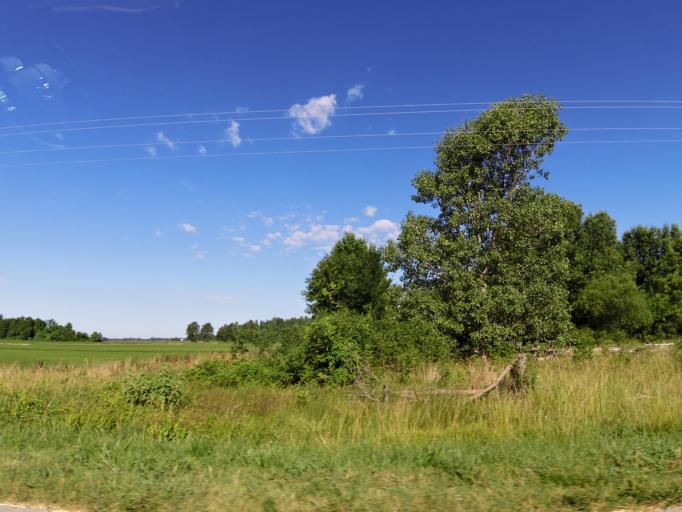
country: US
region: Arkansas
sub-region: Clay County
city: Corning
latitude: 36.5816
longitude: -90.5206
